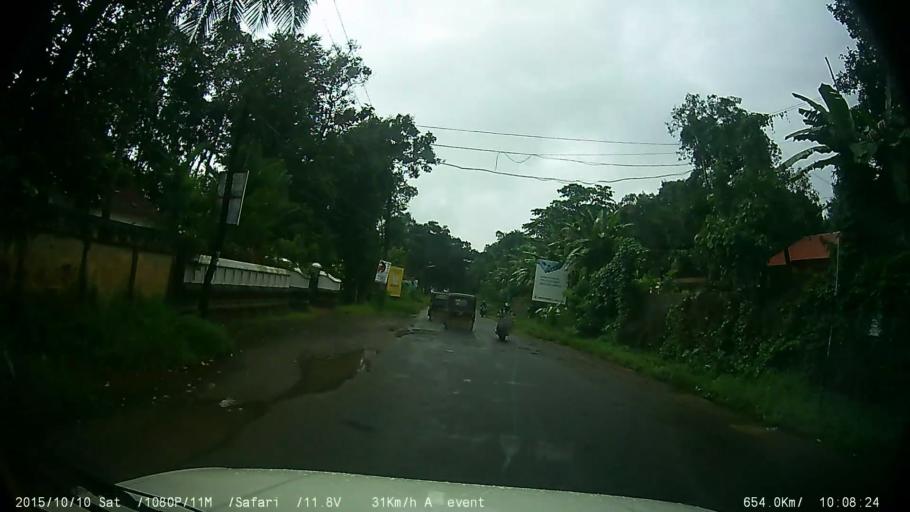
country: IN
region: Kerala
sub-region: Kottayam
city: Kottayam
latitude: 9.6384
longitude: 76.5303
